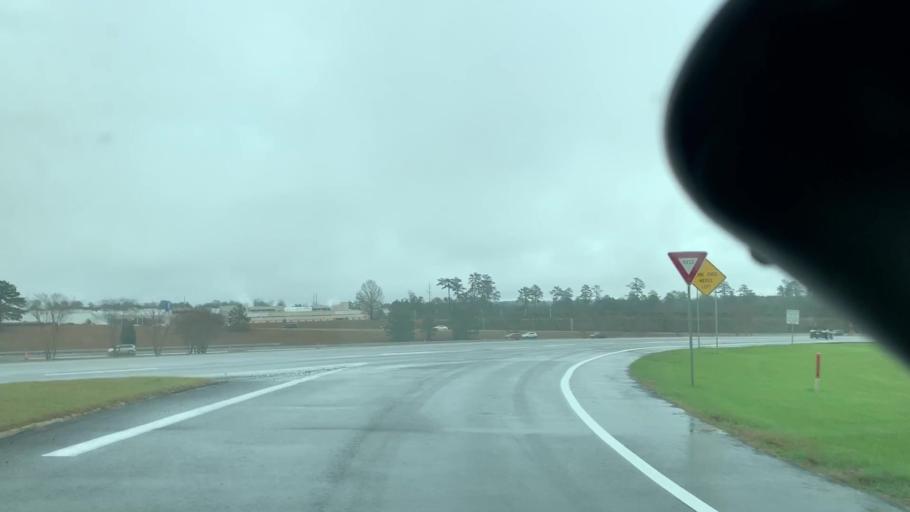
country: US
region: South Carolina
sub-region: Richland County
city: Dentsville
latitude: 34.1345
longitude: -80.9651
